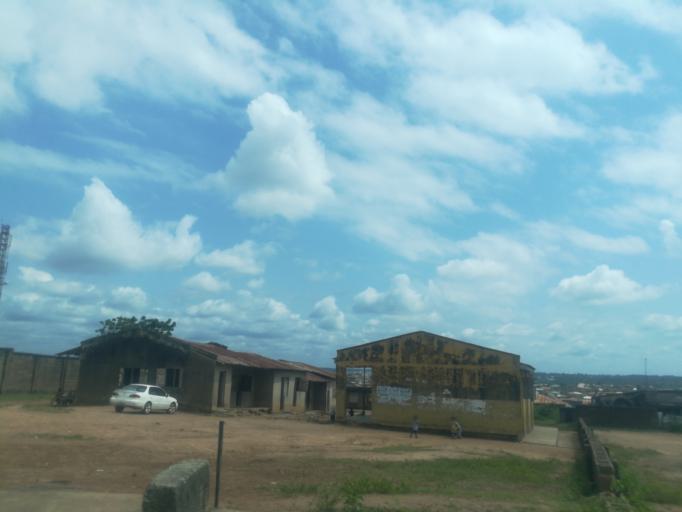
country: NG
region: Oyo
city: Egbeda
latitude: 7.4180
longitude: 4.0017
